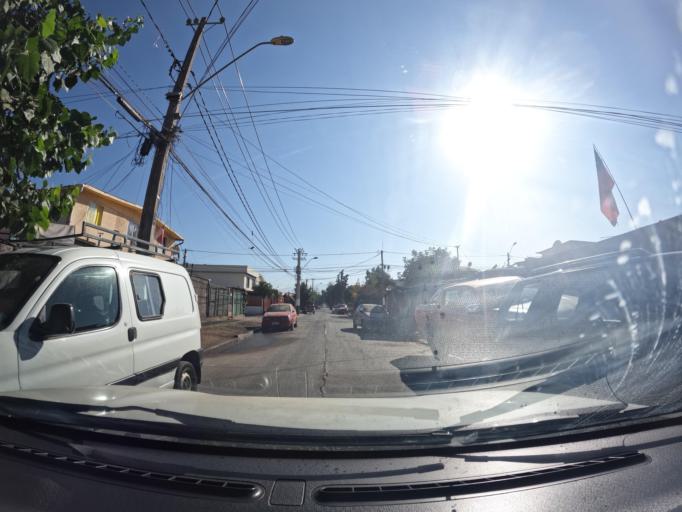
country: CL
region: Santiago Metropolitan
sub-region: Provincia de Santiago
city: Villa Presidente Frei, Nunoa, Santiago, Chile
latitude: -33.4804
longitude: -70.5754
